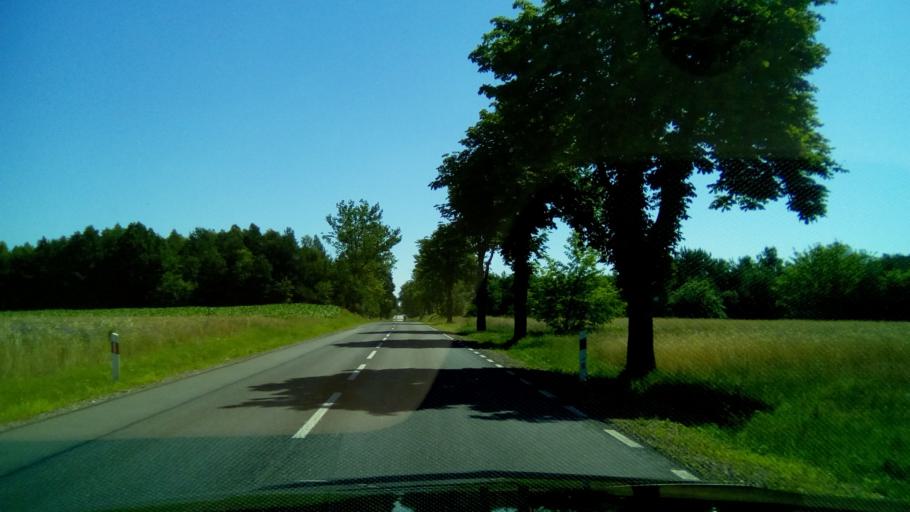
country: PL
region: Masovian Voivodeship
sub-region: Powiat przysuski
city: Odrzywol
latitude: 51.5193
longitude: 20.5031
